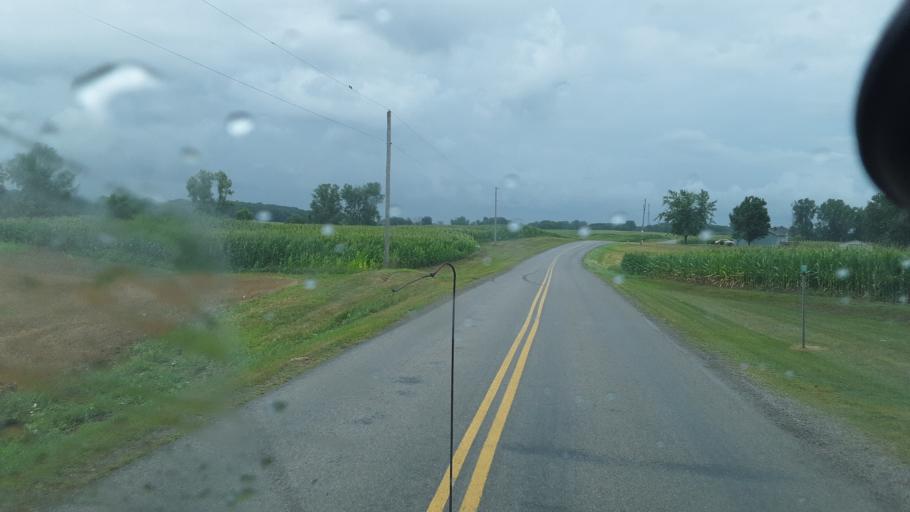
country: US
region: Indiana
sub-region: Steuben County
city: Fremont
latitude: 41.6497
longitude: -84.7916
